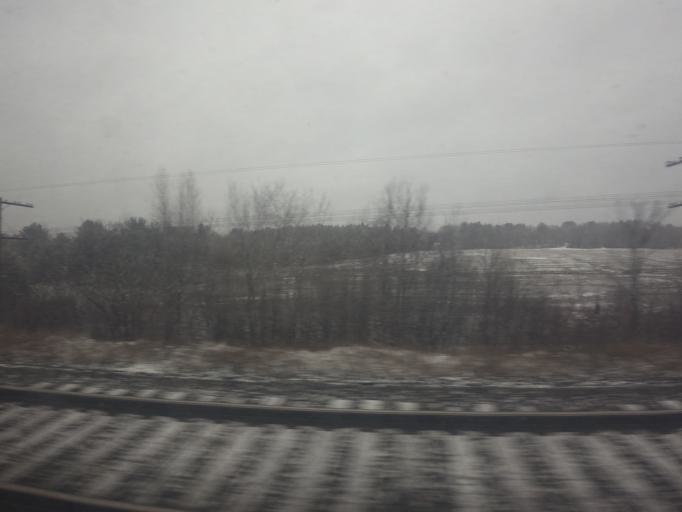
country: US
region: New York
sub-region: Jefferson County
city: Alexandria Bay
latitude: 44.5036
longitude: -75.8571
